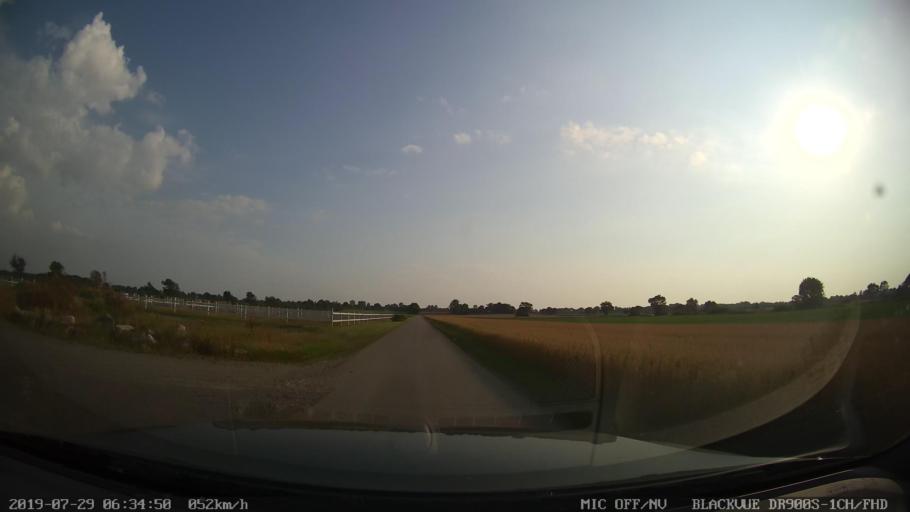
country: SE
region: Skane
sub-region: Helsingborg
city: Odakra
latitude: 56.1174
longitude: 12.7229
